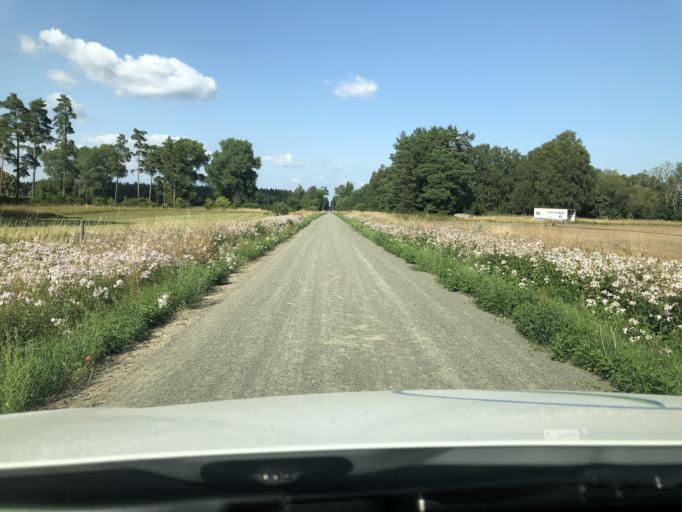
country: SE
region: Skane
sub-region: Kristianstads Kommun
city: Norra Asum
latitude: 55.9105
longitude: 14.1124
